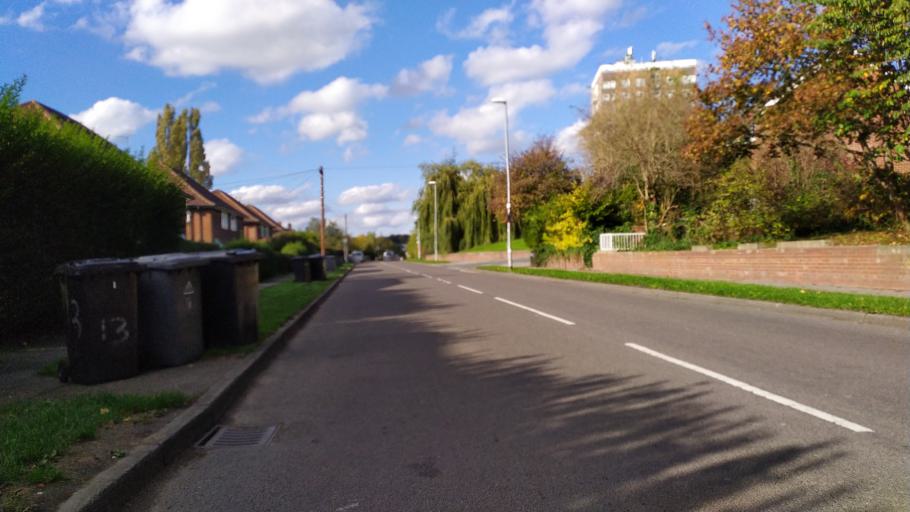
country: GB
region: England
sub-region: City and Borough of Leeds
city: Leeds
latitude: 53.8179
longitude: -1.5902
